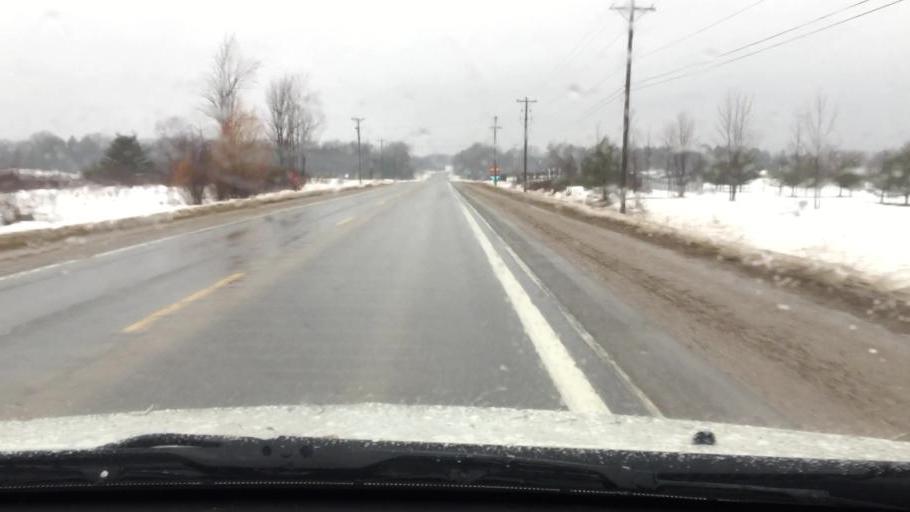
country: US
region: Michigan
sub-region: Charlevoix County
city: Charlevoix
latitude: 45.2774
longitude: -85.2262
